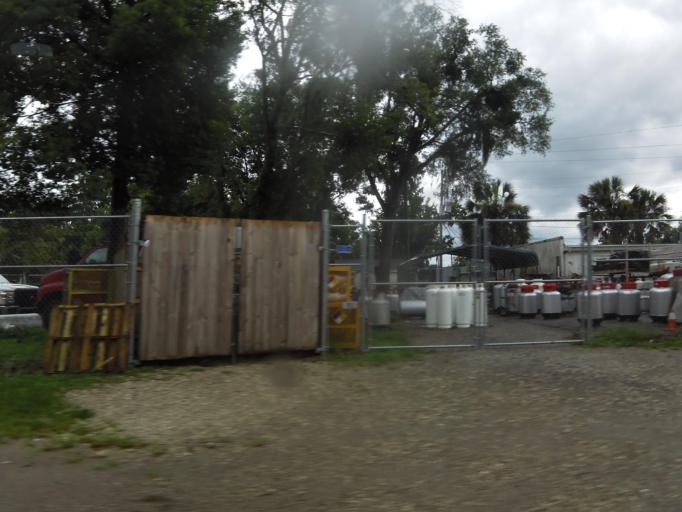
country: US
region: Florida
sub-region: Duval County
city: Jacksonville
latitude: 30.4651
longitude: -81.6327
